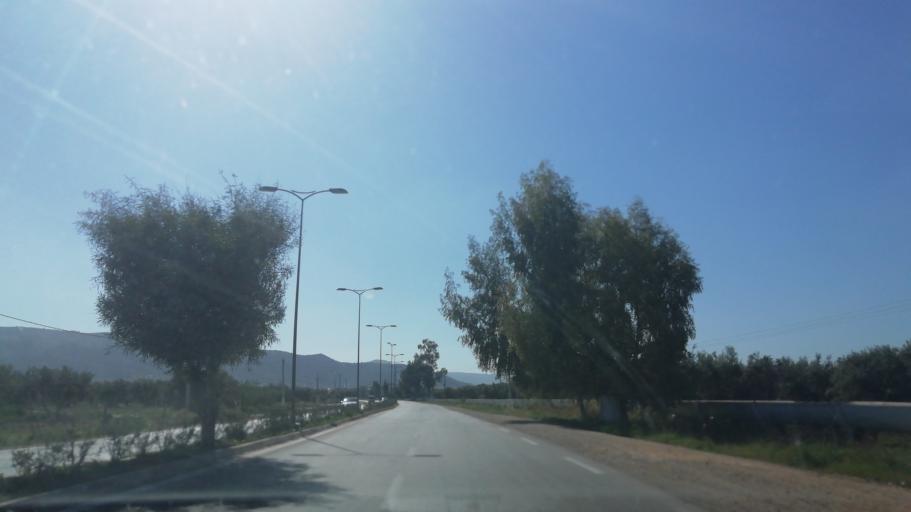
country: DZ
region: Mascara
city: Sig
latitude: 35.5371
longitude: -0.2038
